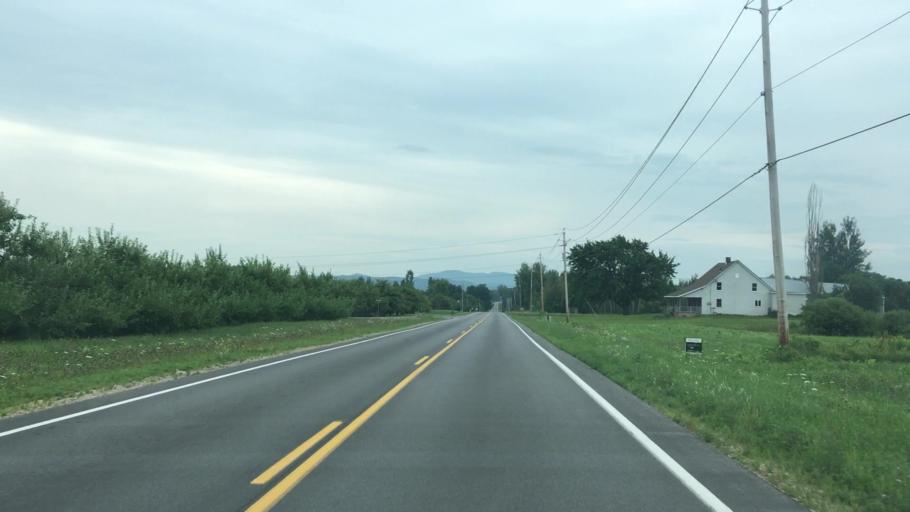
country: US
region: New York
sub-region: Clinton County
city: Peru
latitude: 44.5989
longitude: -73.5737
